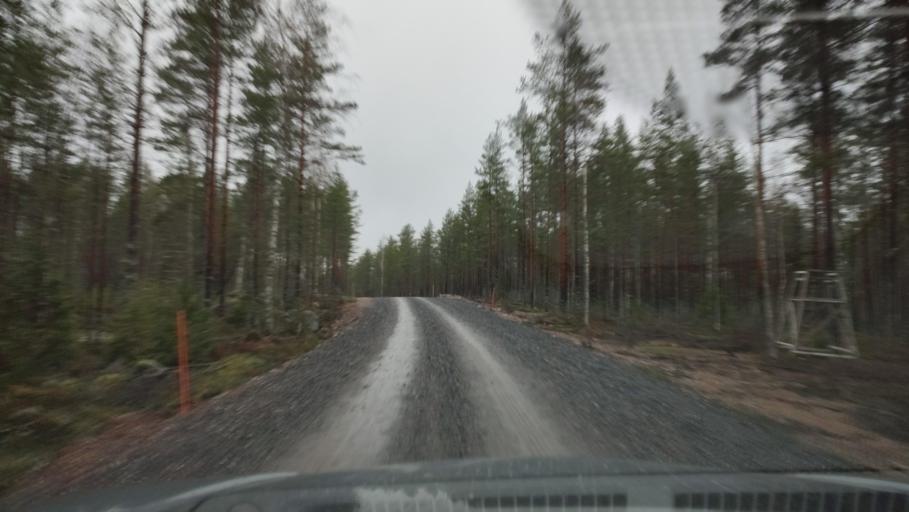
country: FI
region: Southern Ostrobothnia
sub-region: Suupohja
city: Karijoki
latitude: 62.1557
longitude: 21.6173
